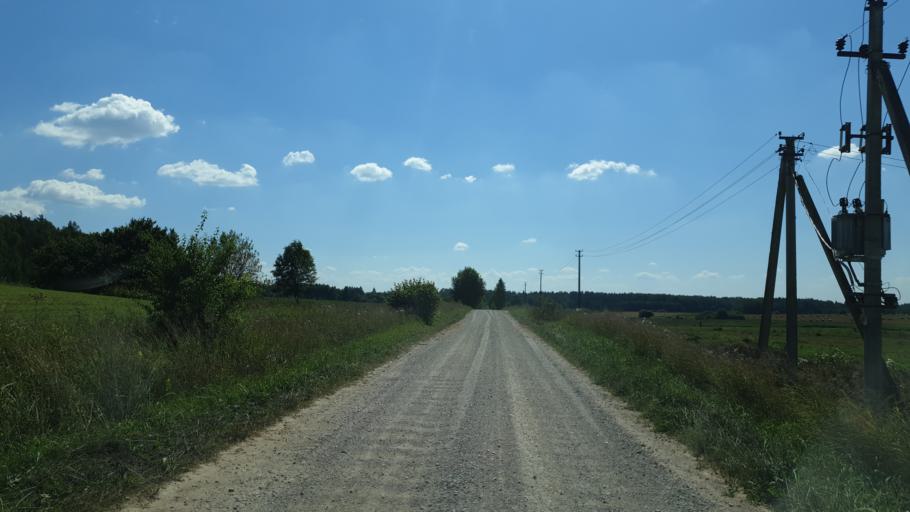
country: LT
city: Sirvintos
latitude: 54.9085
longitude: 24.9114
